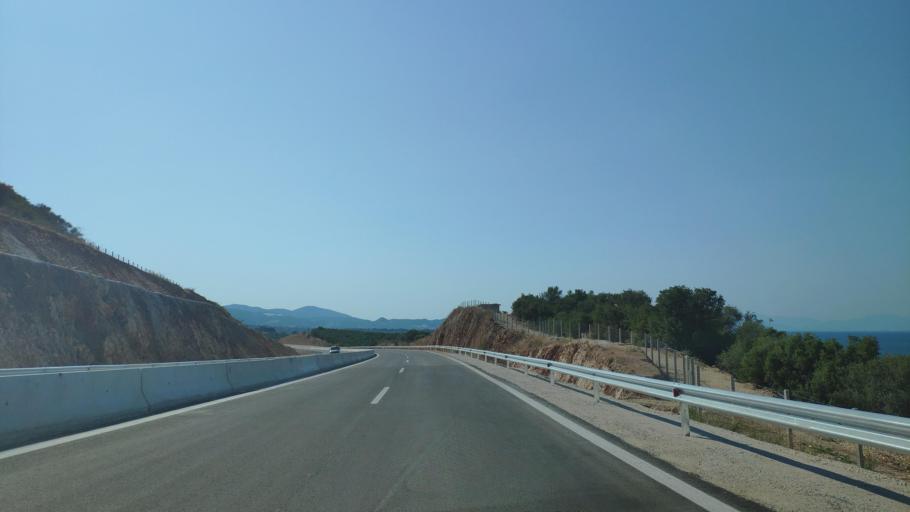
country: GR
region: West Greece
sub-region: Nomos Aitolias kai Akarnanias
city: Amfilochia
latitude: 38.8637
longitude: 21.0769
